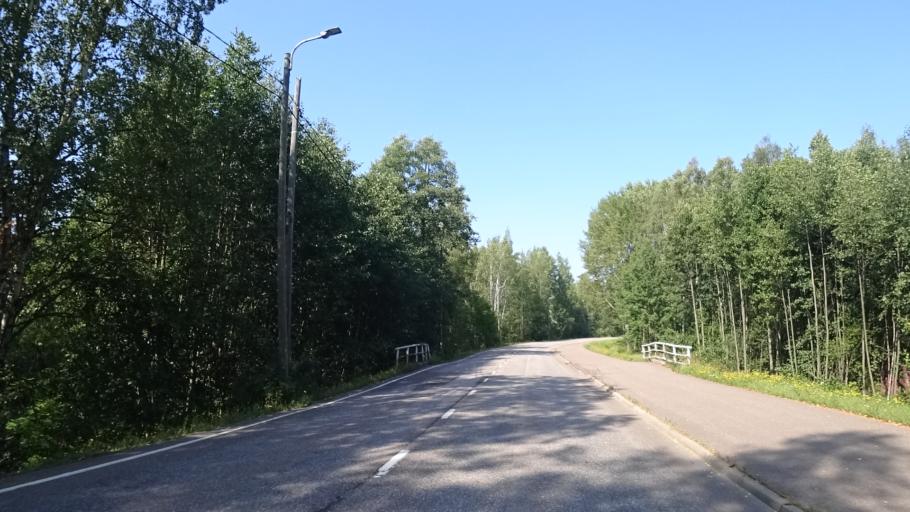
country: FI
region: Kymenlaakso
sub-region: Kotka-Hamina
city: Karhula
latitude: 60.5043
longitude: 26.9483
